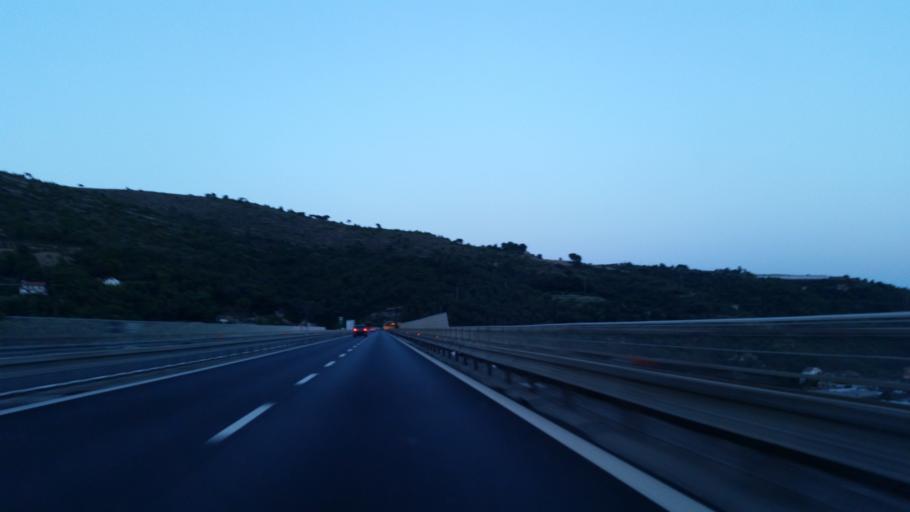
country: IT
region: Liguria
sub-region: Provincia di Imperia
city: Camporosso
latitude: 43.8017
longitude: 7.6273
